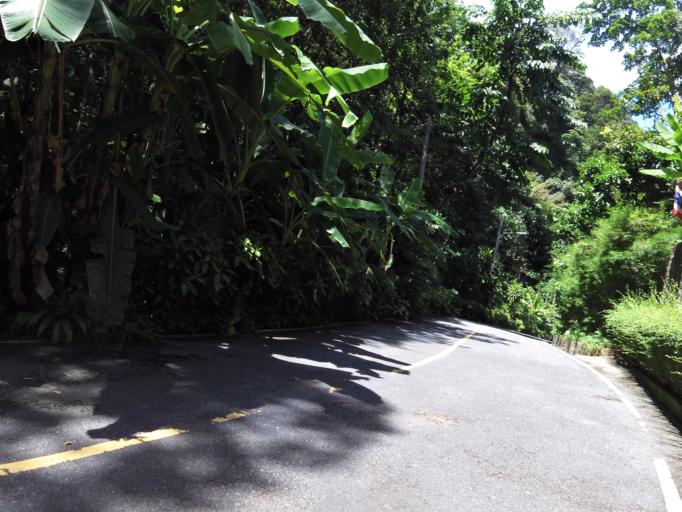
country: TH
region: Phuket
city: Ban Karon
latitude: 7.8441
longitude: 98.3107
